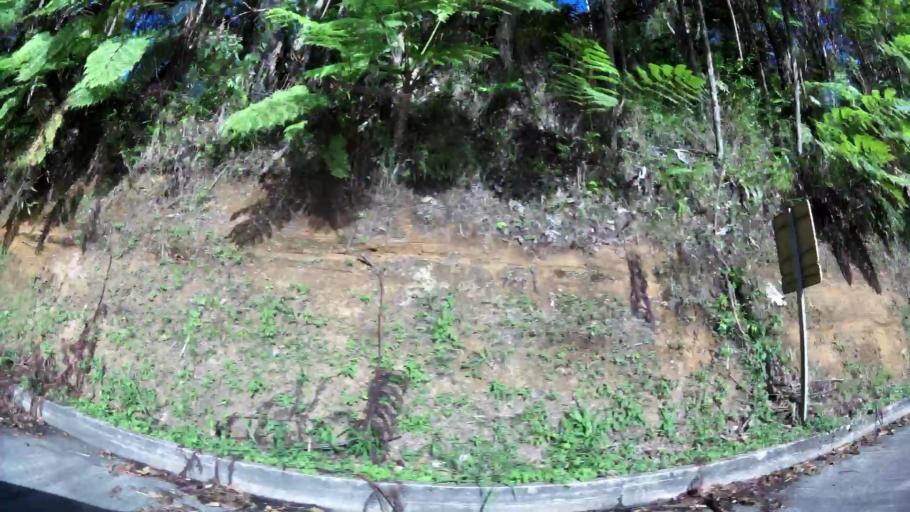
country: MQ
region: Martinique
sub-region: Martinique
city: Saint-Joseph
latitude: 14.6866
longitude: -61.0851
